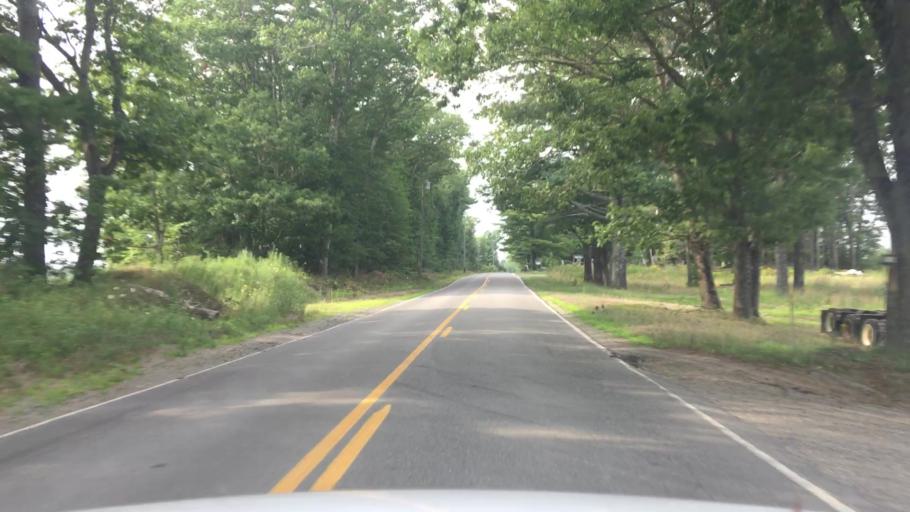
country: US
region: Maine
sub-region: Knox County
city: Washington
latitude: 44.2191
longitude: -69.3862
